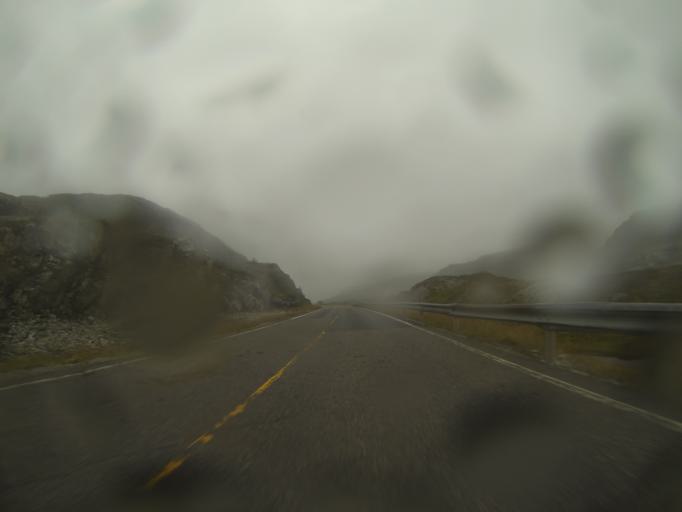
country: NO
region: Vest-Agder
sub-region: Sirdal
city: Tonstad
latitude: 58.9135
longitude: 6.7397
